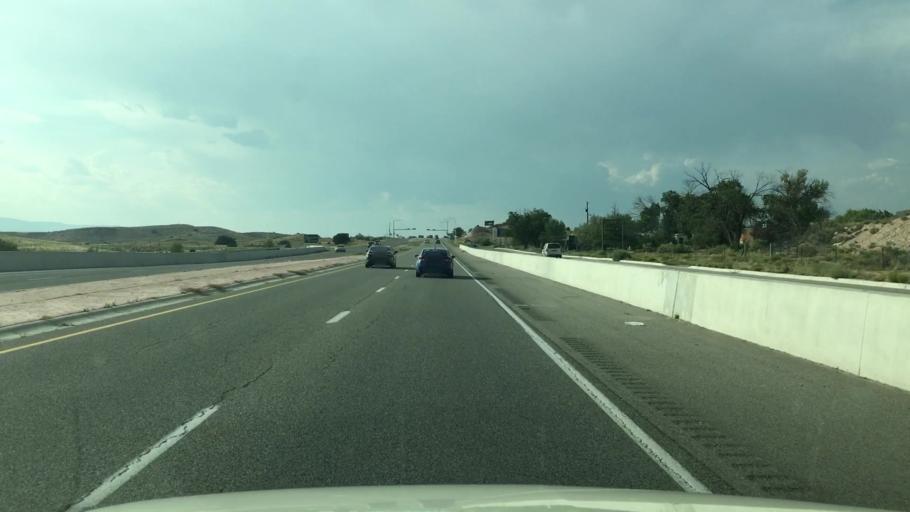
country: US
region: New Mexico
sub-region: Santa Fe County
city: El Valle de Arroyo Seco
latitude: 35.9715
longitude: -106.0401
